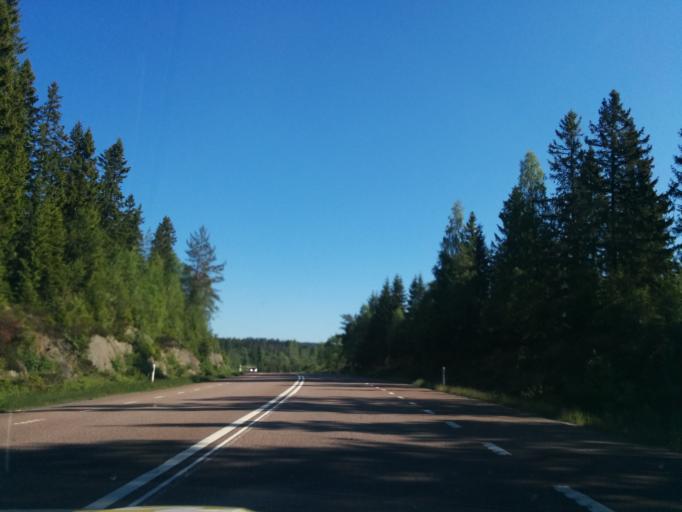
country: SE
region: Vaesternorrland
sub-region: Haernoesands Kommun
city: Haernoesand
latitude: 62.6910
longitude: 17.8518
